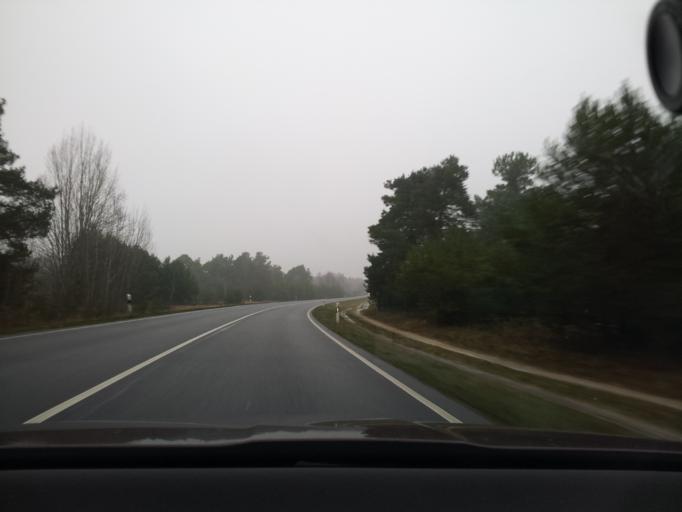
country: DE
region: Brandenburg
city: Langewahl
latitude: 52.3454
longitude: 14.1002
